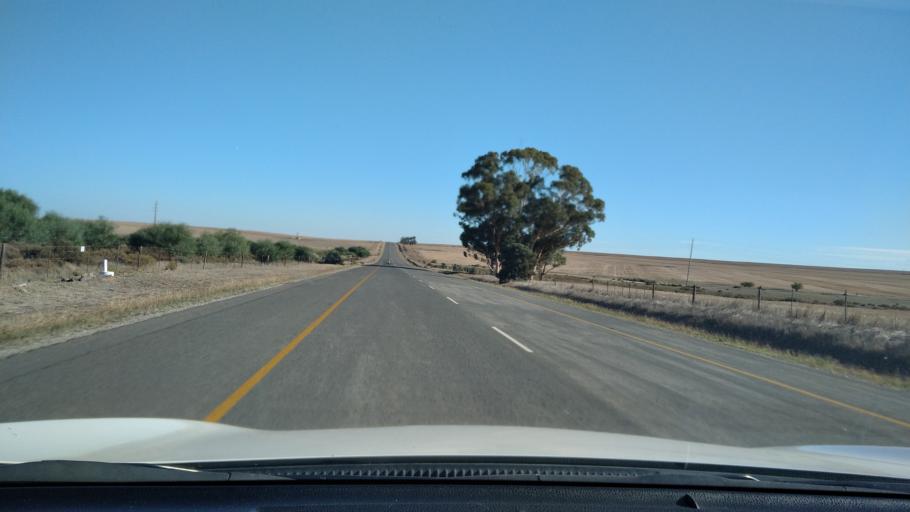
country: ZA
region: Western Cape
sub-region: West Coast District Municipality
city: Malmesbury
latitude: -33.3451
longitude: 18.6385
